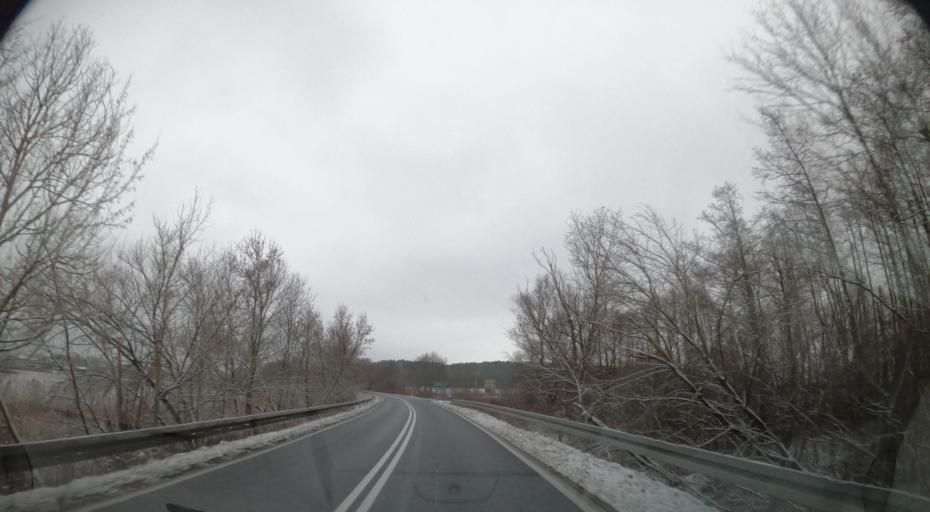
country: PL
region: Masovian Voivodeship
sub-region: Powiat plocki
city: Nowy Duninow
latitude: 52.5817
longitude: 19.5307
